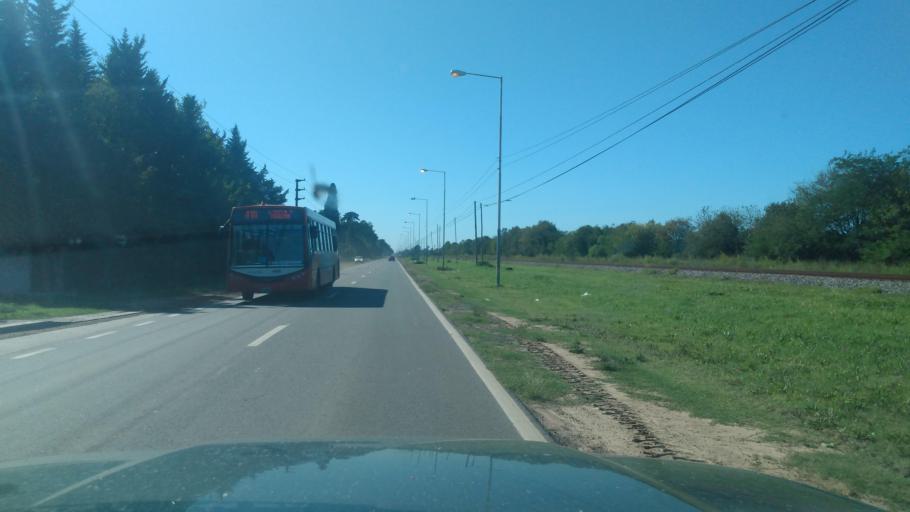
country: AR
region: Buenos Aires
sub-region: Partido de General Rodriguez
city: General Rodriguez
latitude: -34.5945
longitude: -59.0135
